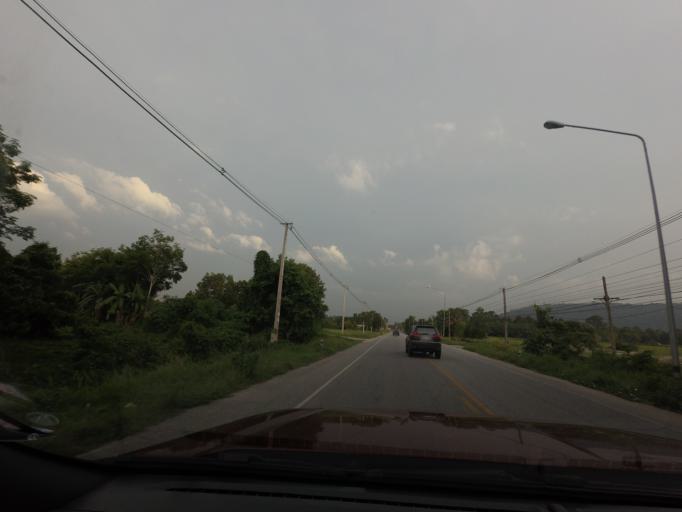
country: TH
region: Pattani
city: Mae Lan
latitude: 6.6268
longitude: 101.1878
